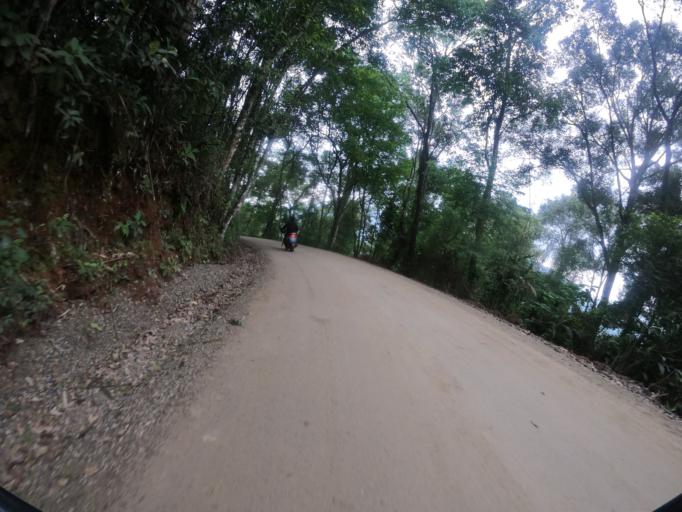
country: TH
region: Chiang Mai
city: Chiang Mai
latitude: 18.8170
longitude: 98.8944
